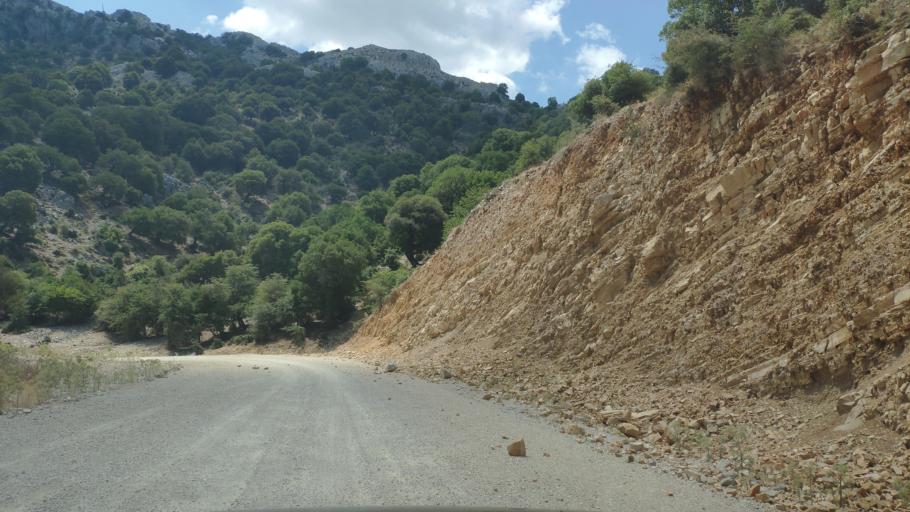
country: GR
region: West Greece
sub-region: Nomos Aitolias kai Akarnanias
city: Monastirakion
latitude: 38.7819
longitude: 20.9854
